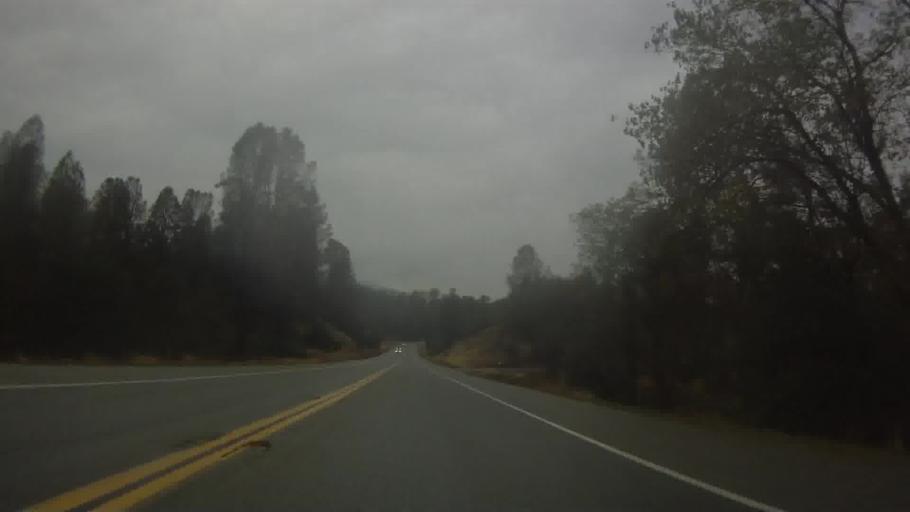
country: US
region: California
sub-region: Shasta County
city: Shasta
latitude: 40.5855
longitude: -122.4505
